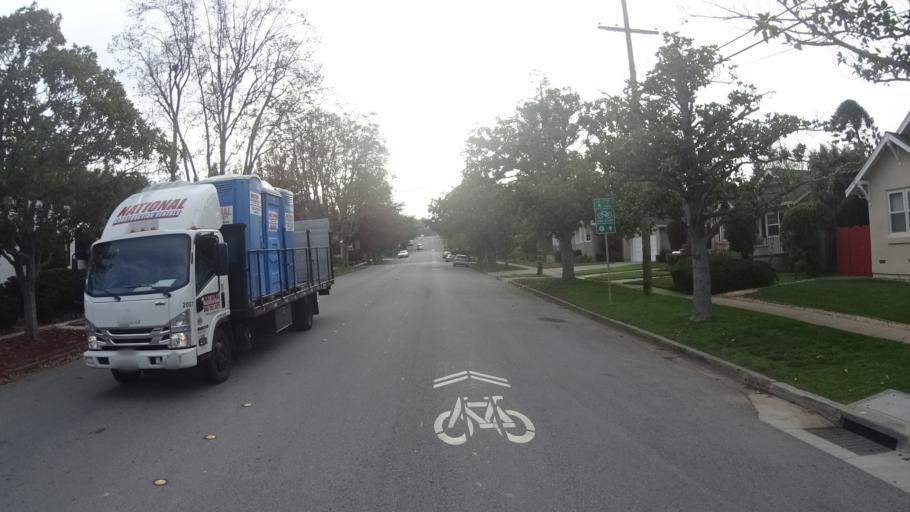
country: US
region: California
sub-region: San Mateo County
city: Burlingame
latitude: 37.5854
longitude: -122.3738
